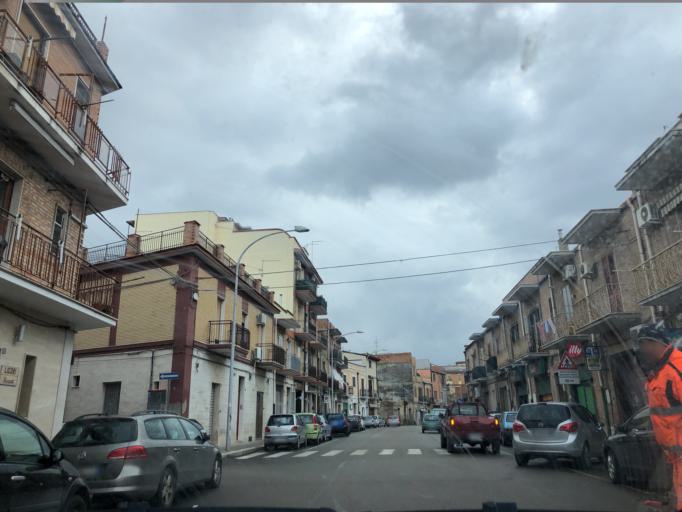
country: IT
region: Apulia
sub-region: Provincia di Foggia
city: Lucera
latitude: 41.5087
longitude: 15.3401
